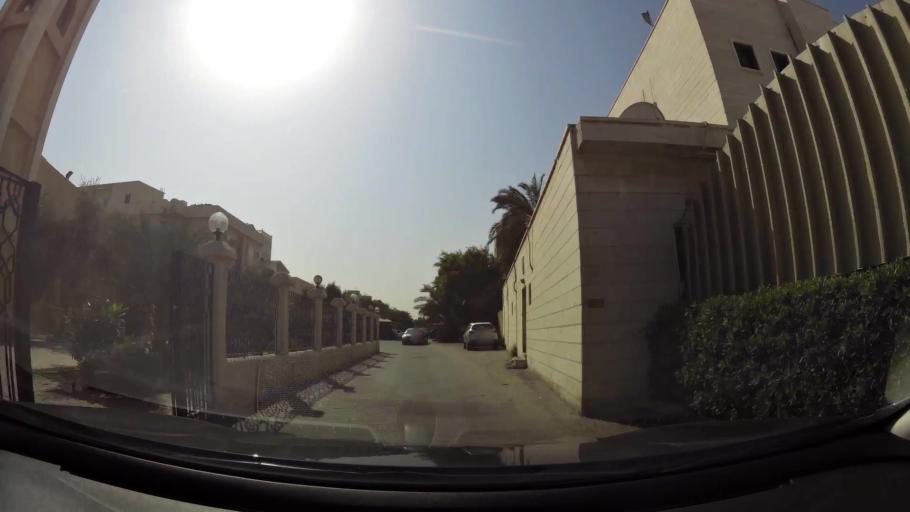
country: KW
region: Muhafazat Hawalli
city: Salwa
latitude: 29.2886
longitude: 48.0843
